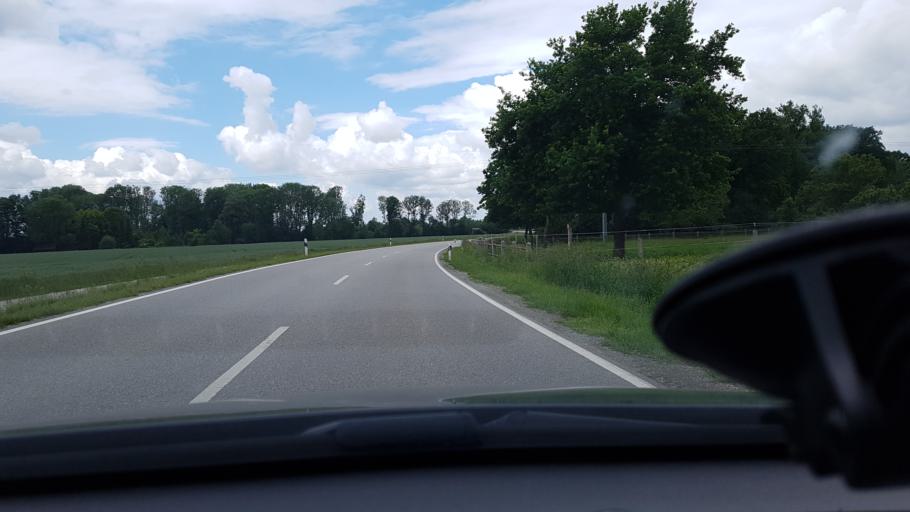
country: DE
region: Bavaria
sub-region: Lower Bavaria
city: Pocking
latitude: 48.4056
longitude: 13.3786
